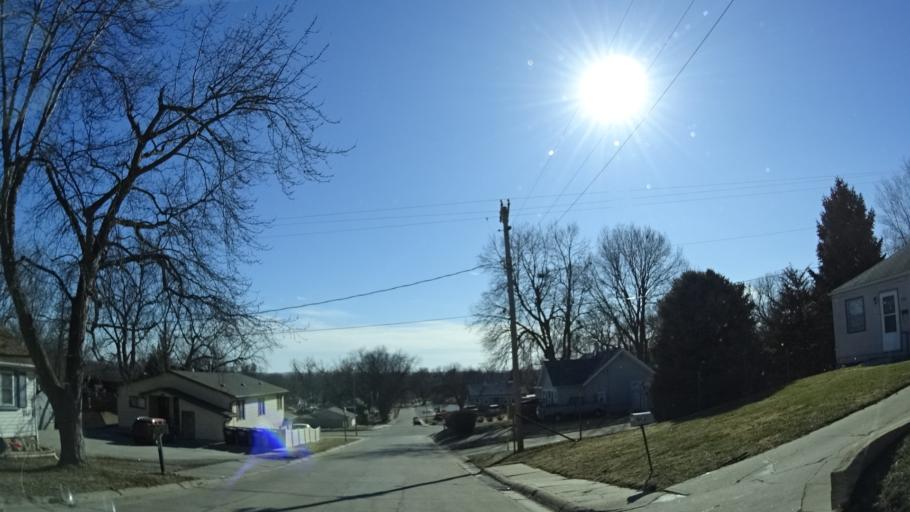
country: US
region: Nebraska
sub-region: Sarpy County
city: Bellevue
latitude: 41.1372
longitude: -95.9028
